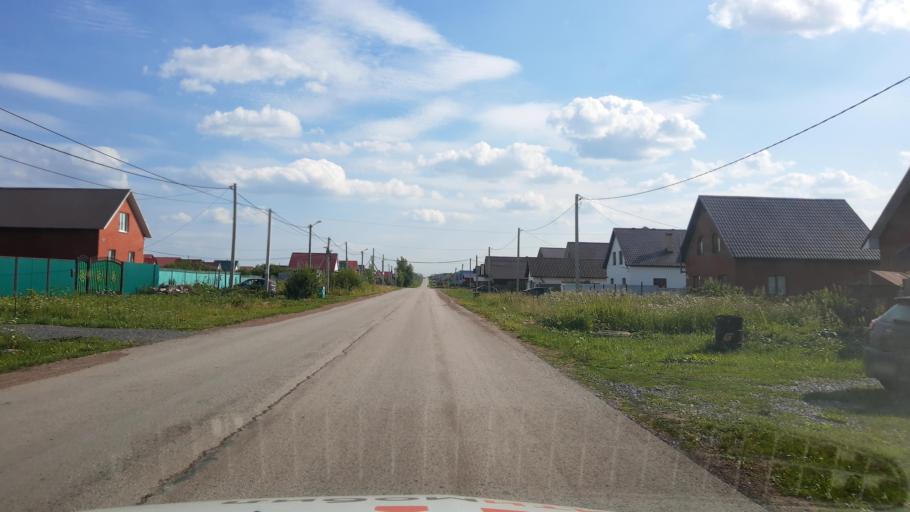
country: RU
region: Bashkortostan
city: Kabakovo
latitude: 54.6624
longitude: 56.2139
